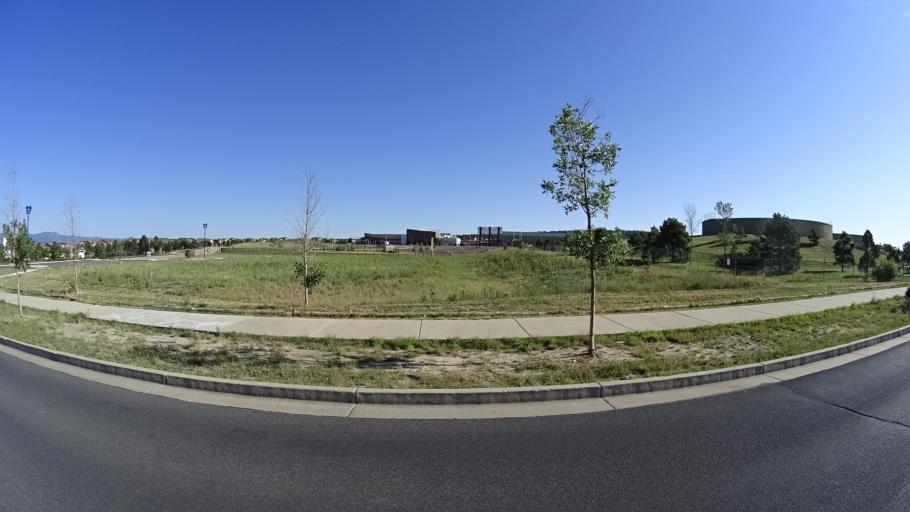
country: US
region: Colorado
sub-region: El Paso County
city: Black Forest
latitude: 38.9712
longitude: -104.7341
